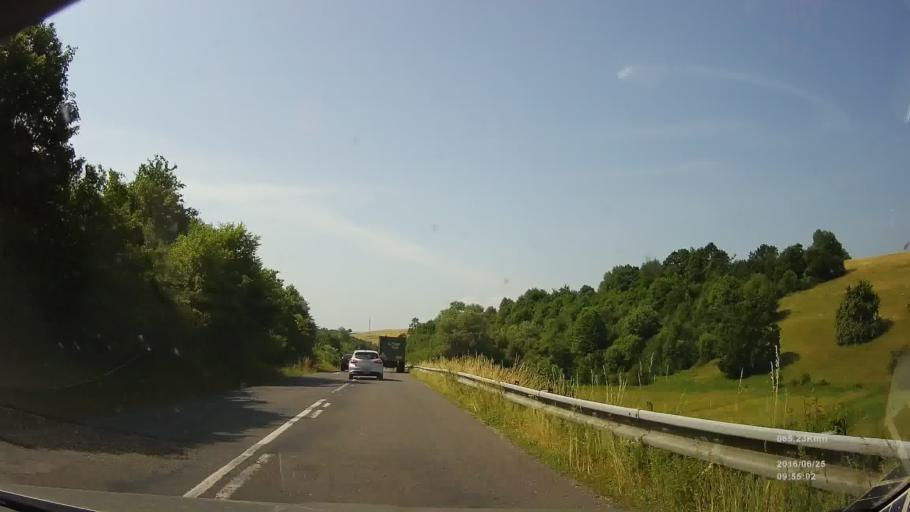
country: SK
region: Banskobystricky
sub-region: Okres Banska Bystrica
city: Banska Bystrica
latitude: 48.6904
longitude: 19.2193
